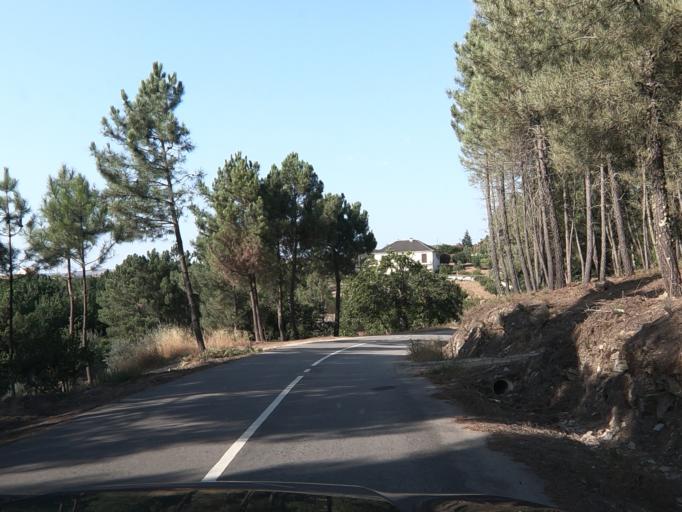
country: PT
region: Vila Real
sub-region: Sabrosa
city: Vilela
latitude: 41.2228
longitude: -7.6353
